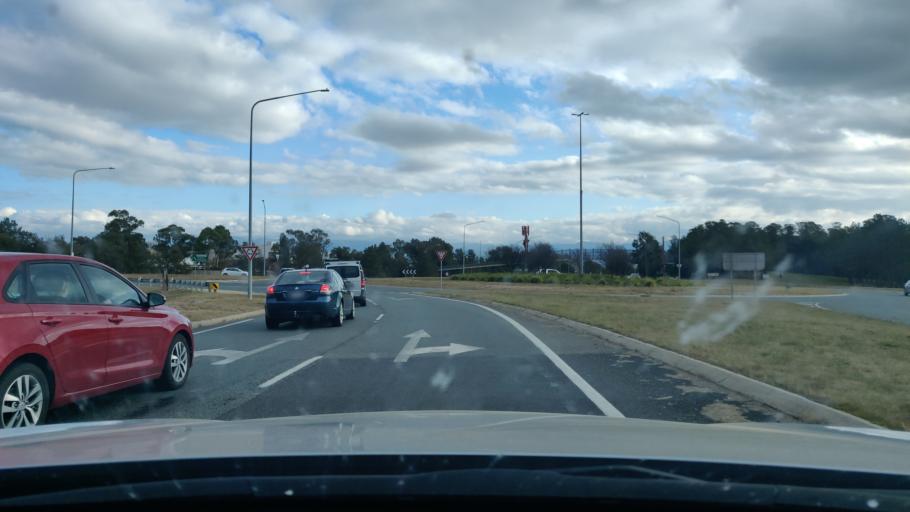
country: AU
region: Australian Capital Territory
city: Macarthur
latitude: -35.4117
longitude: 149.1308
